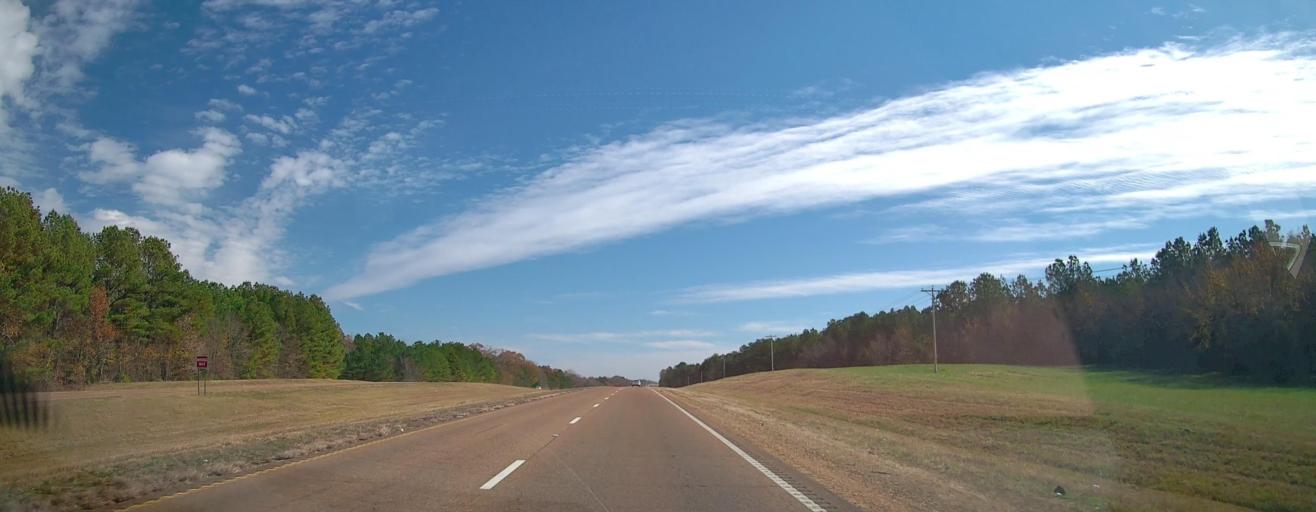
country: US
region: Tennessee
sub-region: Fayette County
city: Piperton
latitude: 34.9563
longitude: -89.5029
